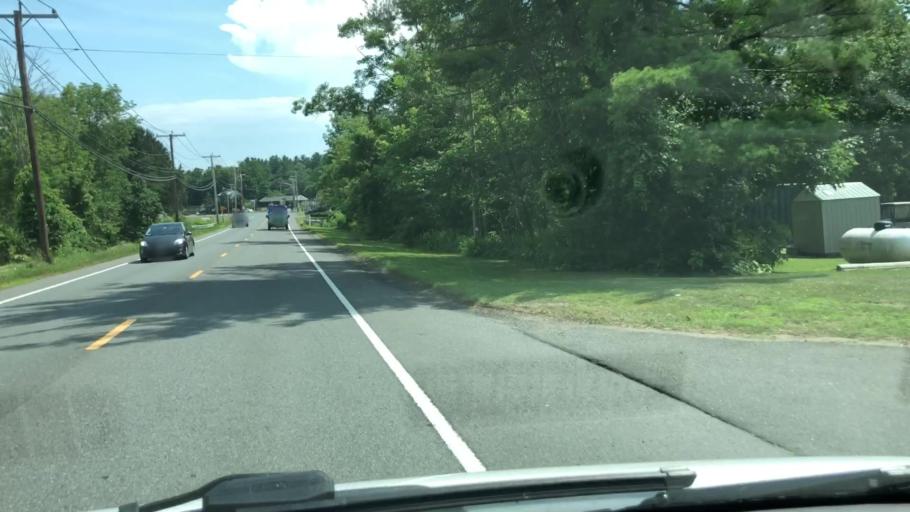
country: US
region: Massachusetts
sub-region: Hampshire County
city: Northampton
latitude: 42.3523
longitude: -72.6908
